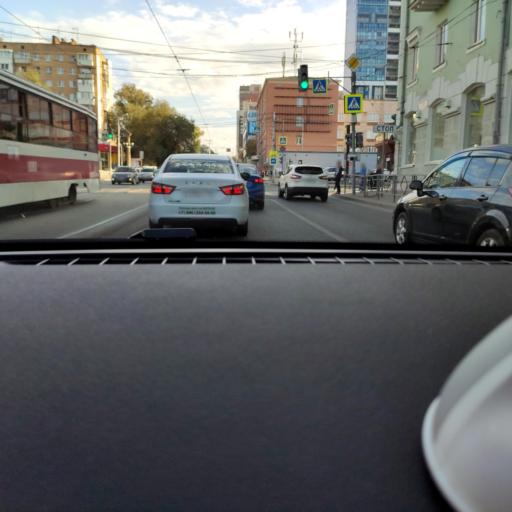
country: RU
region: Samara
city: Samara
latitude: 53.2055
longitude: 50.1231
